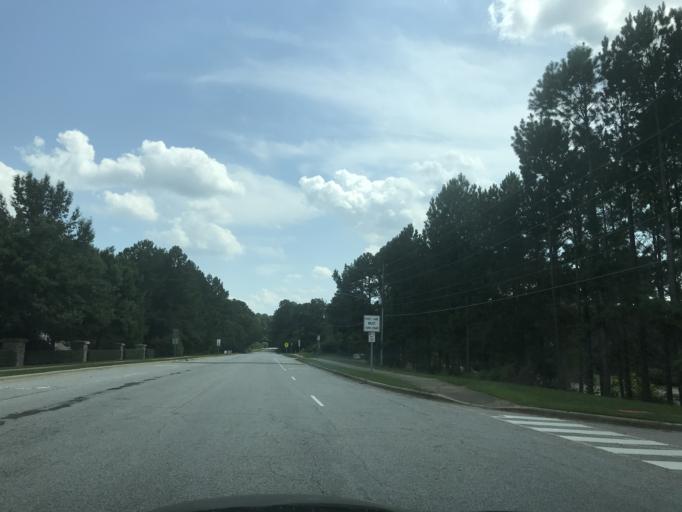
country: US
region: North Carolina
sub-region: Wake County
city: West Raleigh
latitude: 35.8912
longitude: -78.6554
